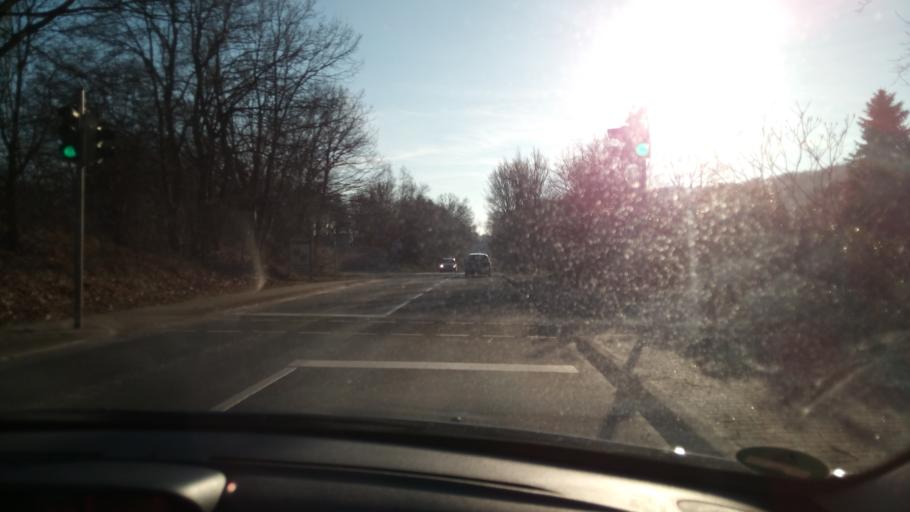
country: DE
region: Schleswig-Holstein
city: Buchen
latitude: 53.4713
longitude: 10.6237
